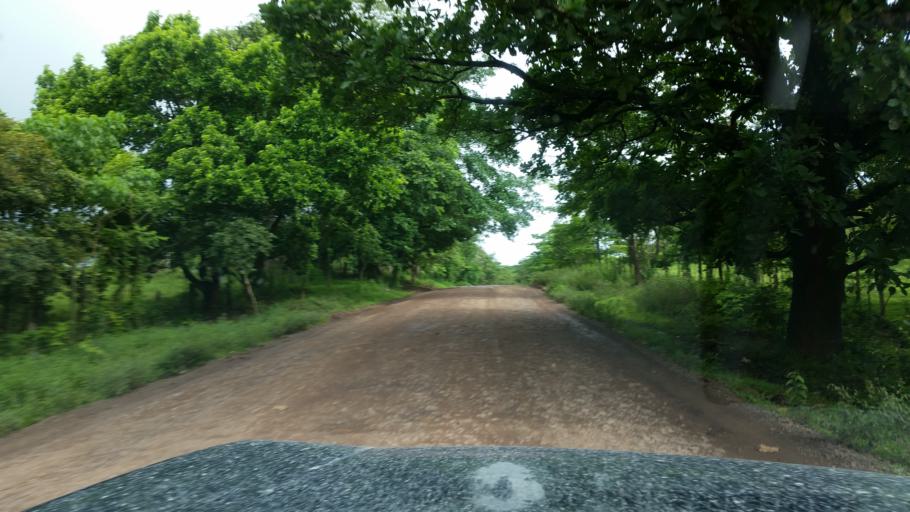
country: NI
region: Atlantico Norte (RAAN)
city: Siuna
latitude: 13.4217
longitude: -84.8531
